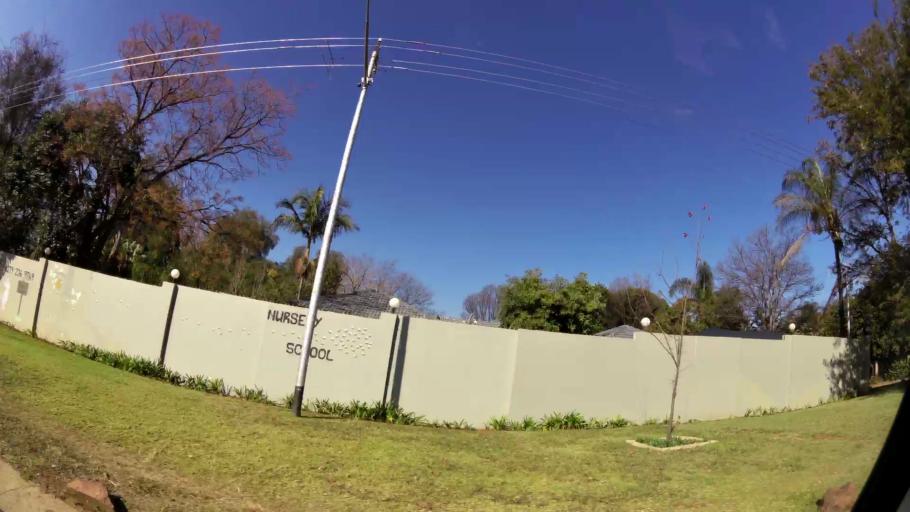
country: ZA
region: Gauteng
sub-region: City of Tshwane Metropolitan Municipality
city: Pretoria
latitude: -25.7846
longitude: 28.2635
